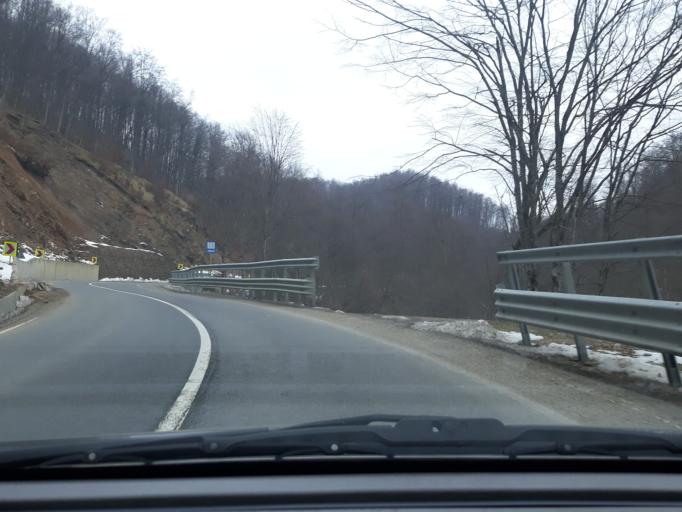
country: RO
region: Bihor
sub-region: Oras Alesd
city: Padurea Neagra
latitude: 47.1215
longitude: 22.4131
